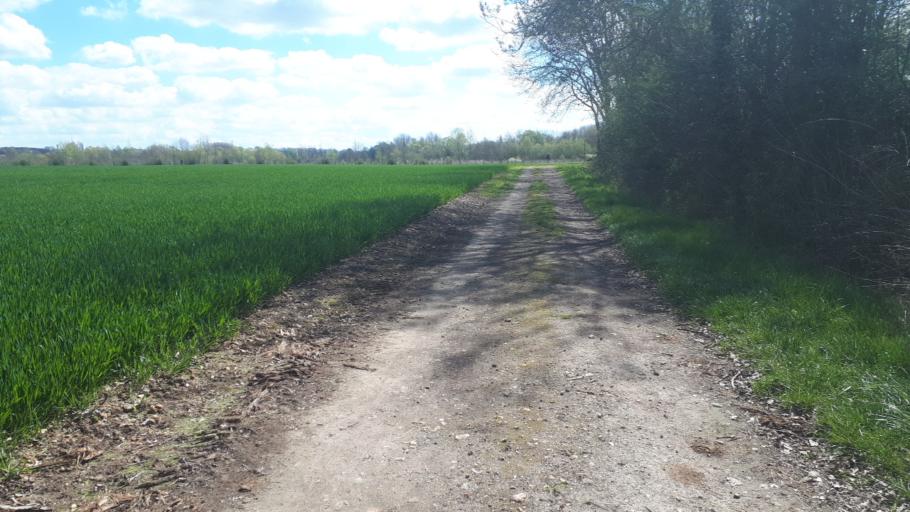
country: FR
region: Centre
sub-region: Departement du Loir-et-Cher
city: Villiers-sur-Loir
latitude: 47.7915
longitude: 0.9913
